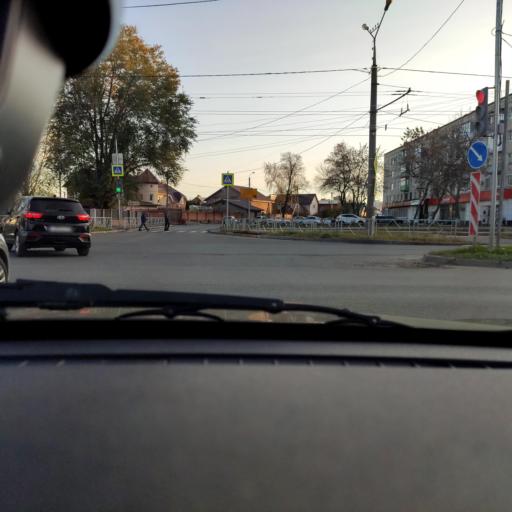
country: RU
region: Samara
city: Tol'yatti
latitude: 53.5315
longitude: 49.4185
